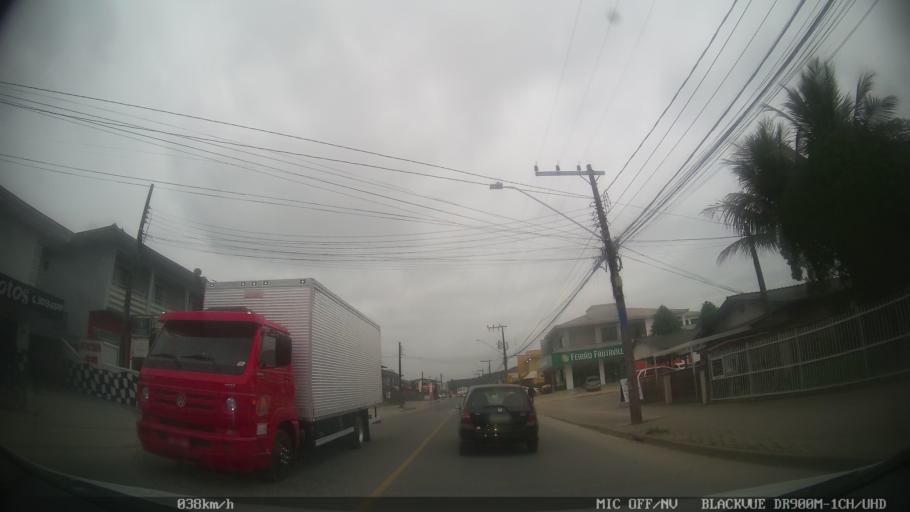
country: BR
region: Santa Catarina
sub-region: Joinville
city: Joinville
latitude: -26.3636
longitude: -48.8295
